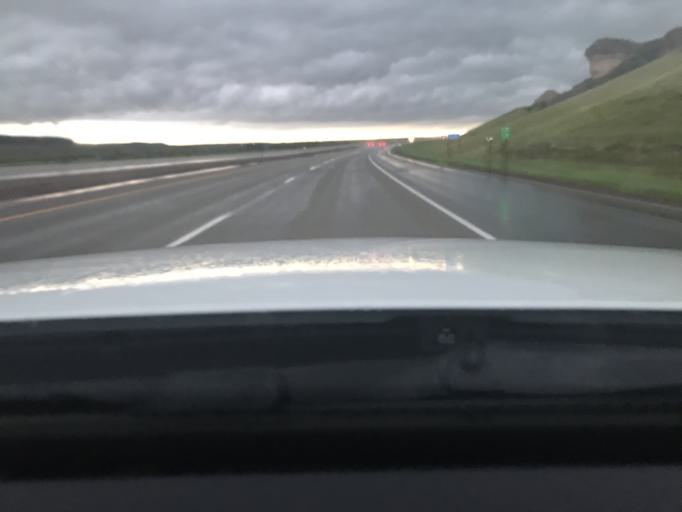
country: US
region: Wyoming
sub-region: Platte County
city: Wheatland
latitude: 41.7769
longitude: -104.7942
